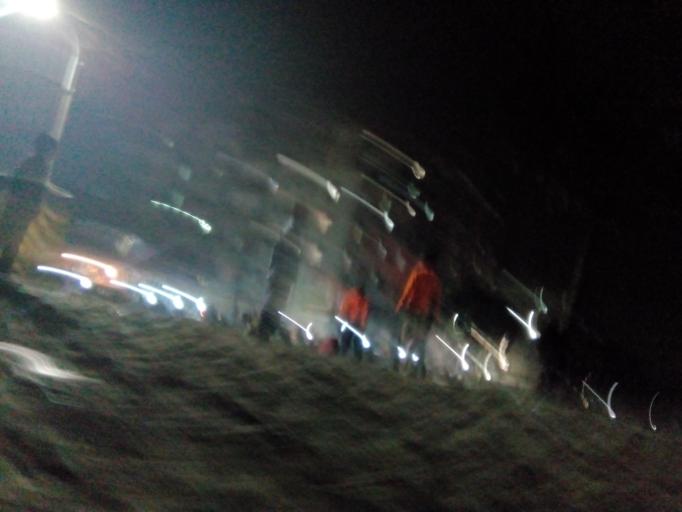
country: BD
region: Dhaka
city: Paltan
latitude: 23.7465
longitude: 90.4203
